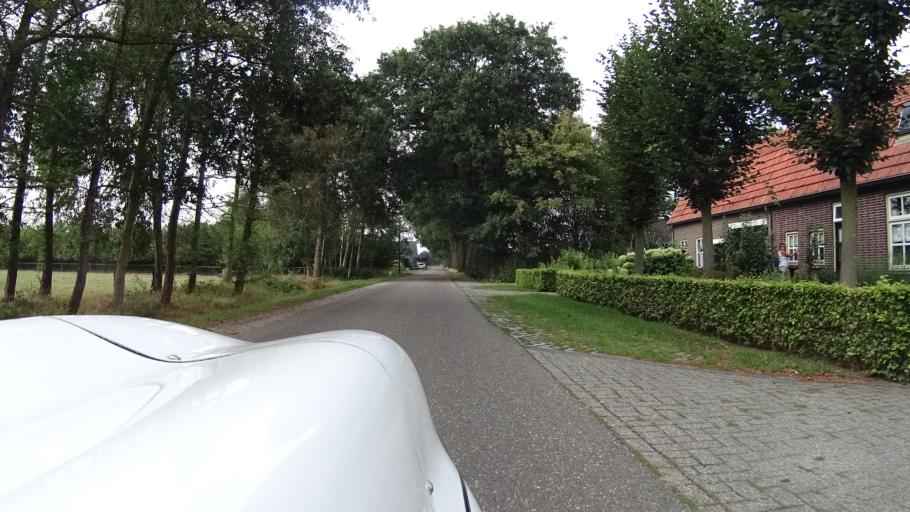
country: NL
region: North Brabant
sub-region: Gemeente Boekel
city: Boekel
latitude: 51.5925
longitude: 5.7203
